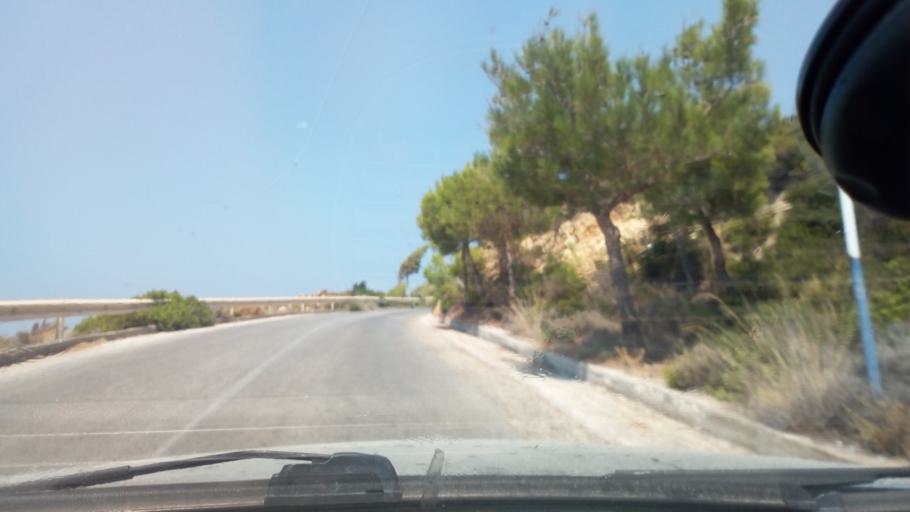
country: GR
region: North Aegean
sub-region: Nomos Samou
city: Agios Kirykos
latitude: 37.6336
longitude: 26.1222
